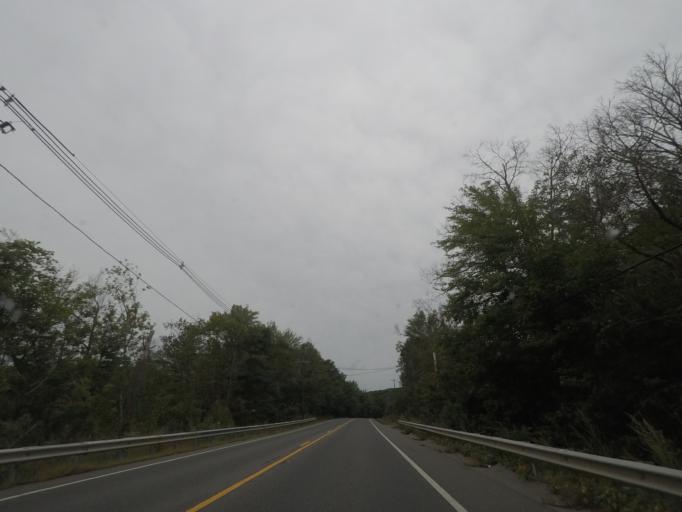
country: US
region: Massachusetts
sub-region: Hampshire County
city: Ware
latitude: 42.2099
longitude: -72.2494
